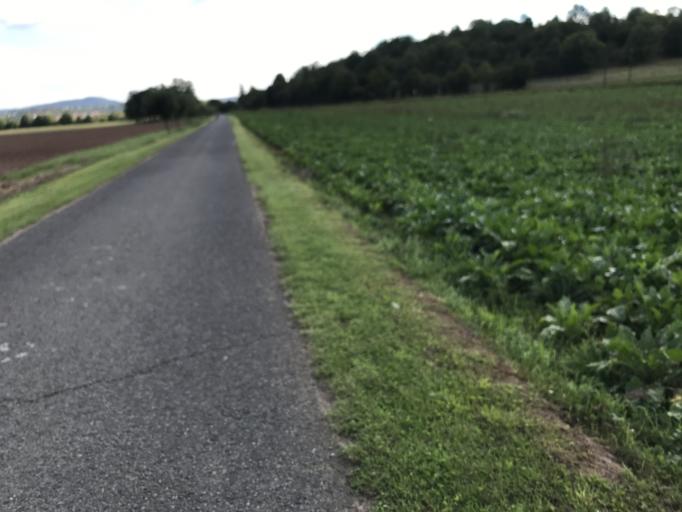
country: DE
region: Hesse
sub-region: Regierungsbezirk Kassel
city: Bad Sooden-Allendorf
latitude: 51.2124
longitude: 9.9973
